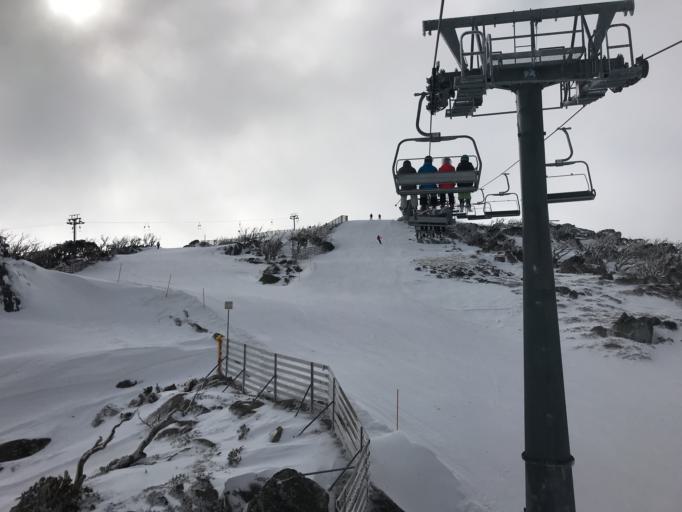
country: AU
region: New South Wales
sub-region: Snowy River
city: Jindabyne
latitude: -36.3821
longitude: 148.3846
